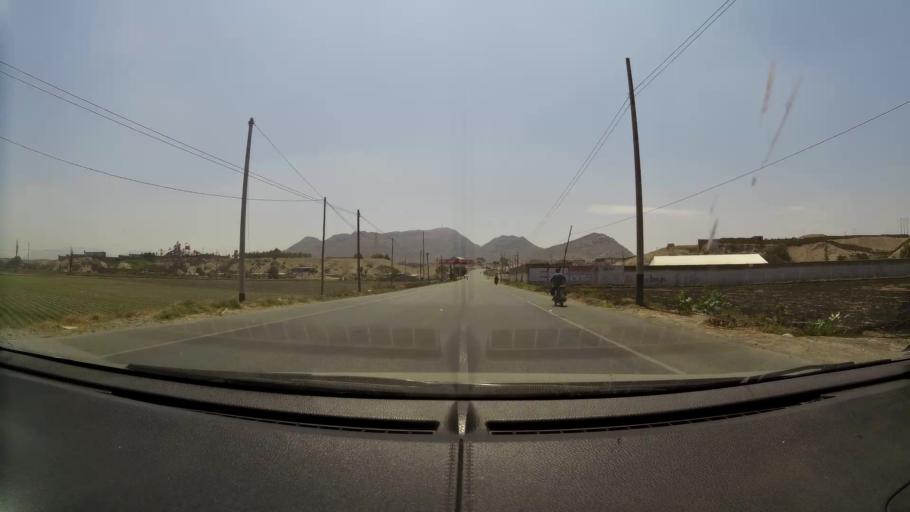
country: PE
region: La Libertad
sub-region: Provincia de Pacasmayo
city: Guadalupe
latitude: -7.3157
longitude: -79.4805
